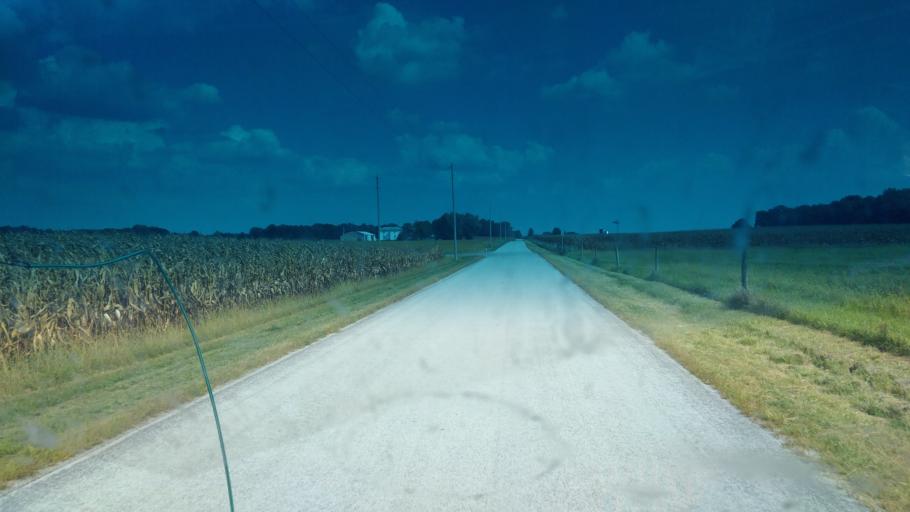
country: US
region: Ohio
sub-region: Hardin County
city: Kenton
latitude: 40.6600
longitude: -83.7071
